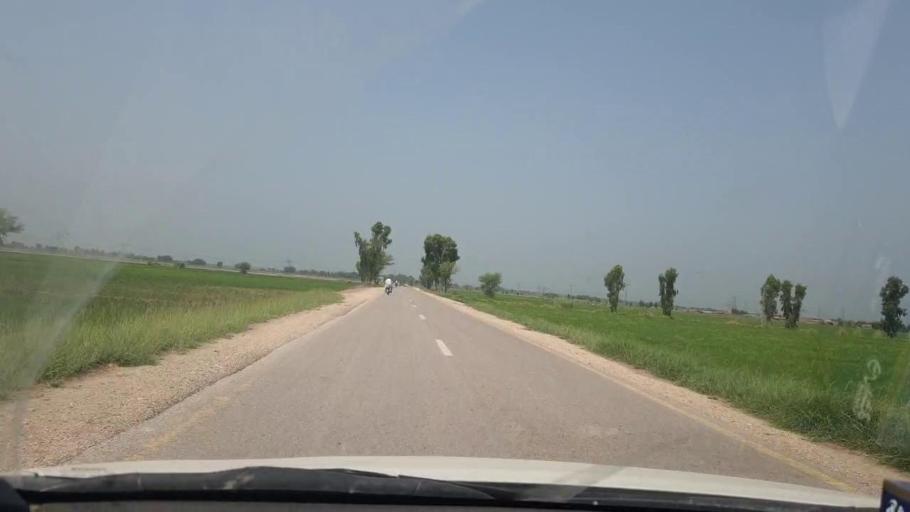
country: PK
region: Sindh
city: Rustam jo Goth
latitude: 27.9595
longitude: 68.7565
